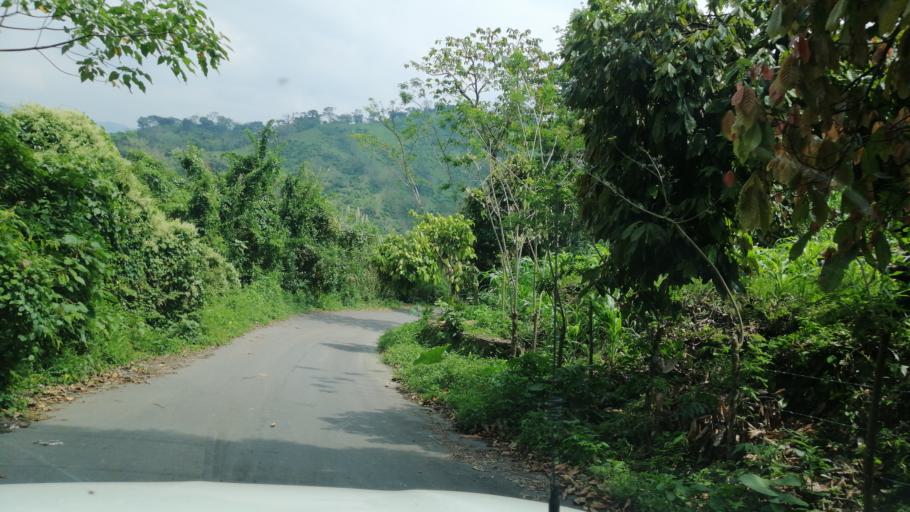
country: MX
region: Chiapas
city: Ostuacan
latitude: 17.3897
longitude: -93.3321
